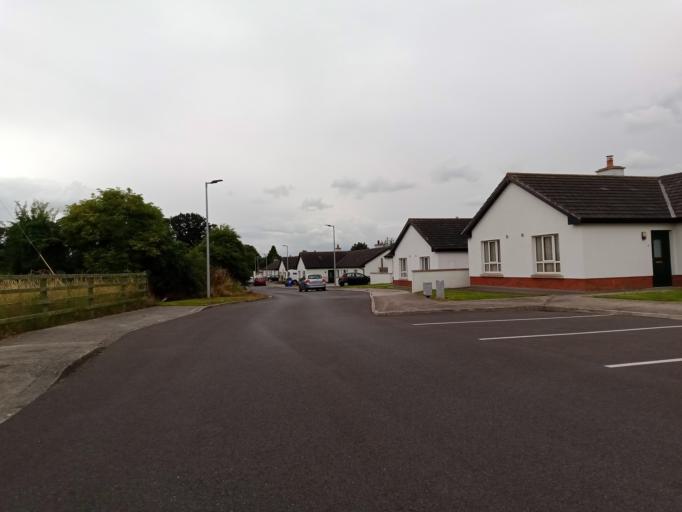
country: IE
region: Leinster
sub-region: Kilkenny
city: Callan
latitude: 52.5491
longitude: -7.3822
